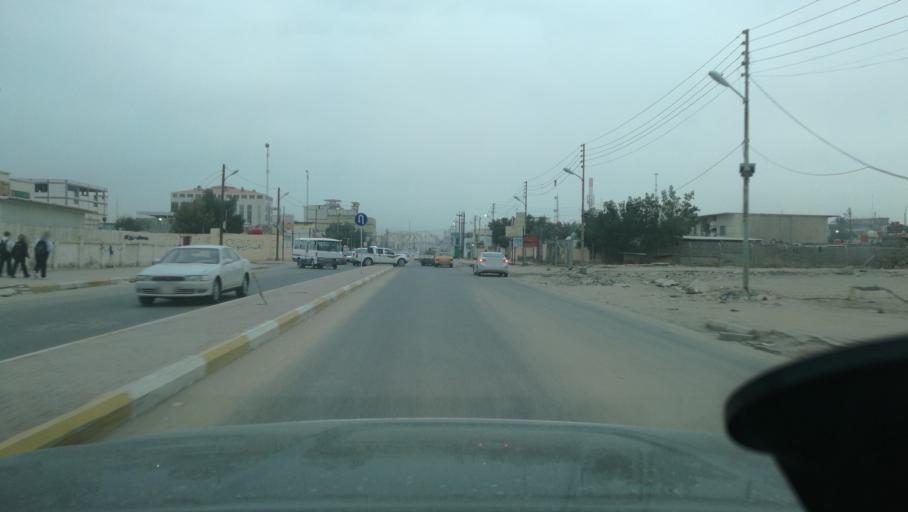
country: IQ
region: Basra Governorate
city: Al Basrah al Qadimah
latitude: 30.5101
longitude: 47.8374
